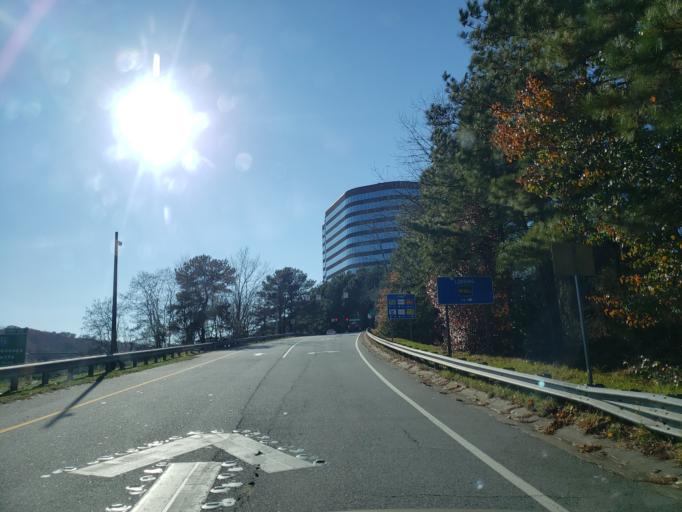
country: US
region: Georgia
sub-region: Fulton County
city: Sandy Springs
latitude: 33.9103
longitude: -84.4284
